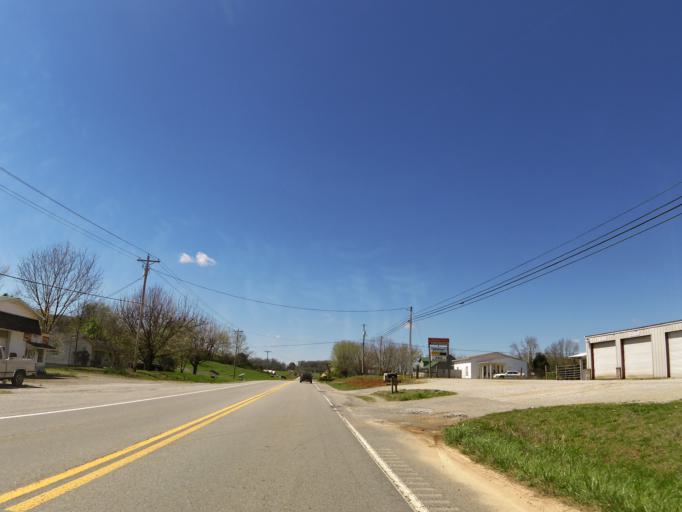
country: US
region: Tennessee
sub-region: White County
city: Sparta
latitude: 35.9456
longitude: -85.5206
